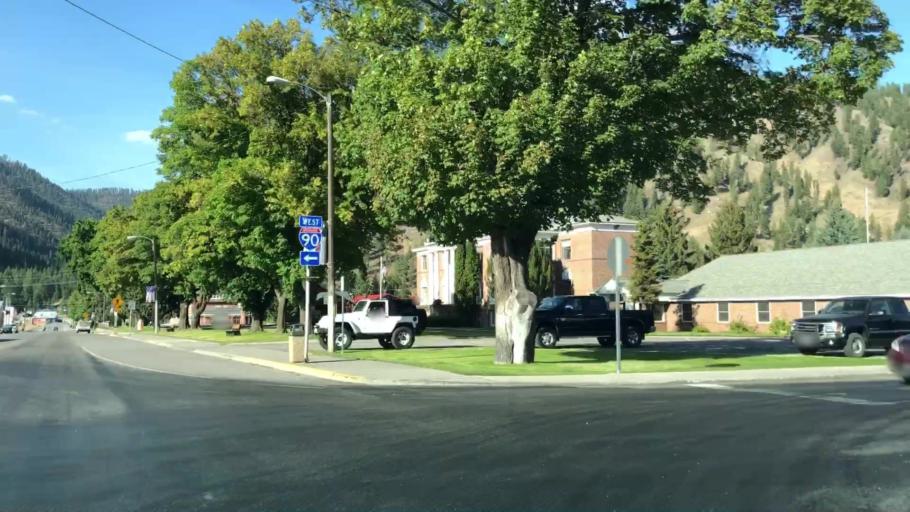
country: US
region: Montana
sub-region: Mineral County
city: Superior
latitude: 47.1924
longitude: -114.8911
